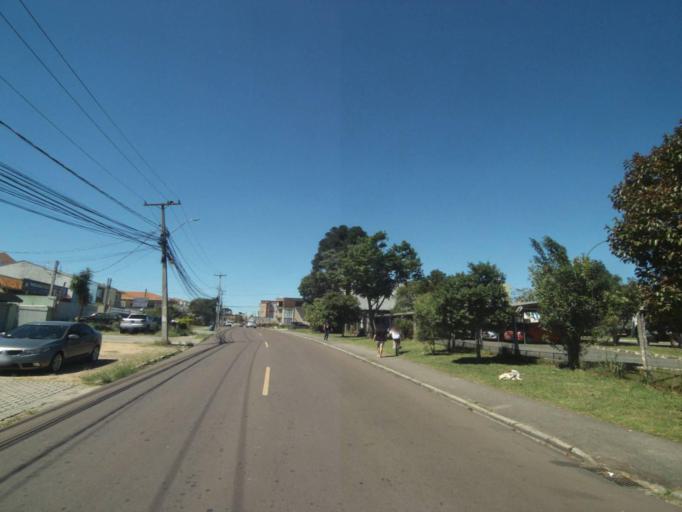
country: BR
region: Parana
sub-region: Curitiba
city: Curitiba
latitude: -25.4807
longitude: -49.3399
